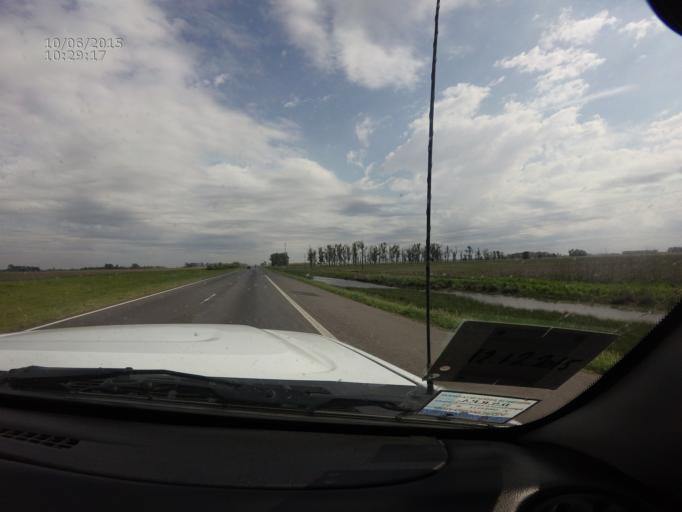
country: AR
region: Buenos Aires
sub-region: Partido de Ramallo
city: Ramallo
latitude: -33.6462
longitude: -59.9746
